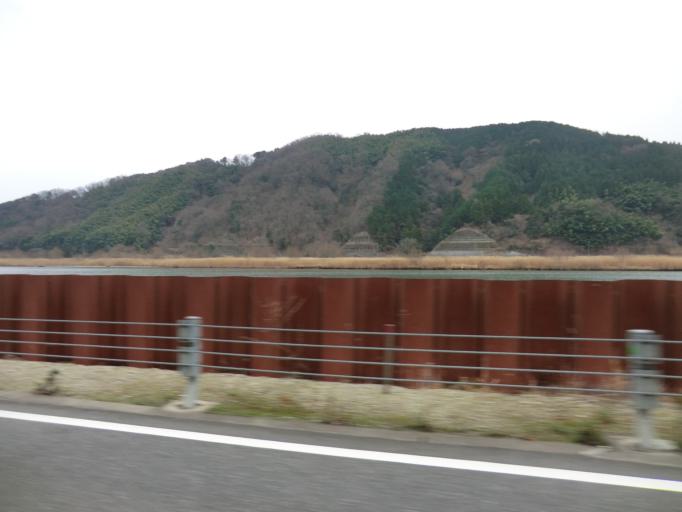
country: JP
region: Hyogo
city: Toyooka
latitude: 35.5985
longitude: 134.8018
